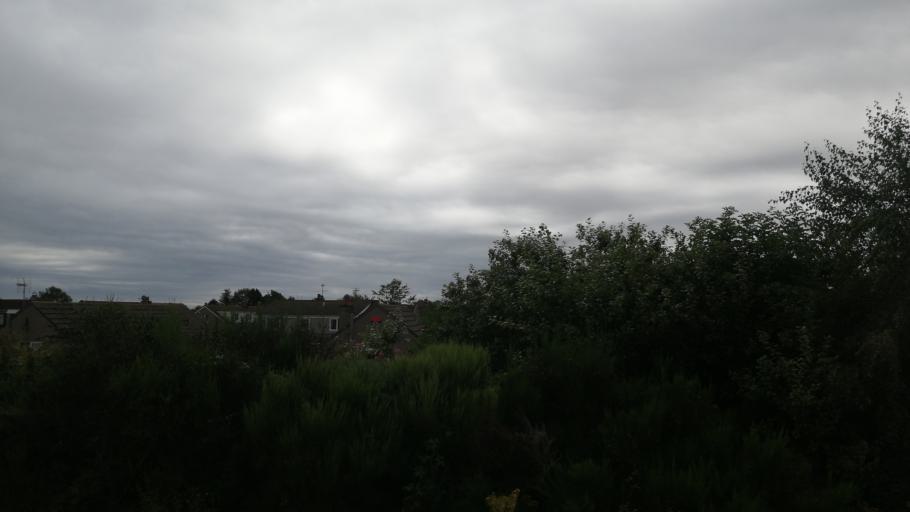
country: GB
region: Scotland
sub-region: Aberdeenshire
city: Stonehaven
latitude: 56.9681
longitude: -2.2231
